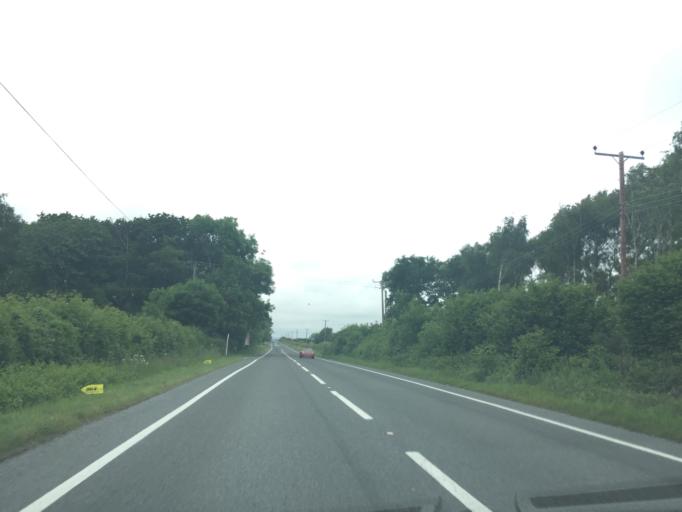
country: GB
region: England
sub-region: Dorset
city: Wareham
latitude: 50.6523
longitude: -2.0809
